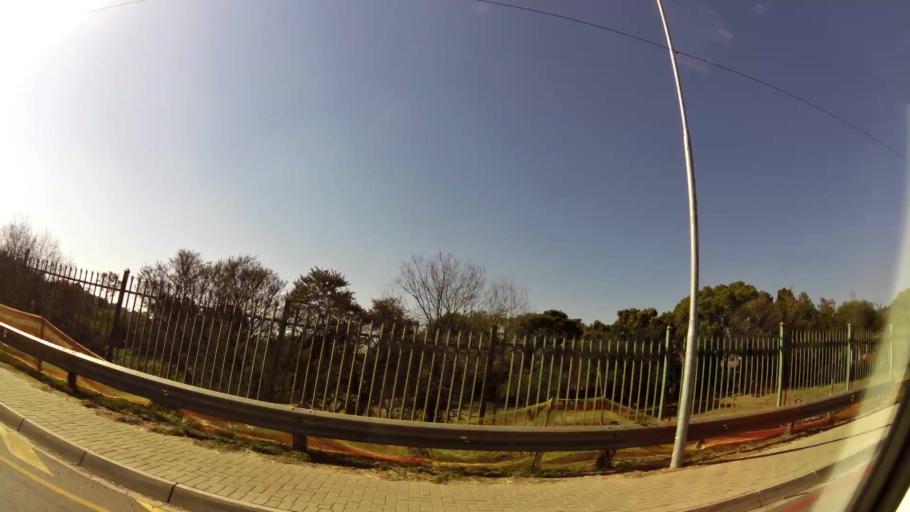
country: ZA
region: Gauteng
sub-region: City of Tshwane Metropolitan Municipality
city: Pretoria
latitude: -25.7822
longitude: 28.2588
